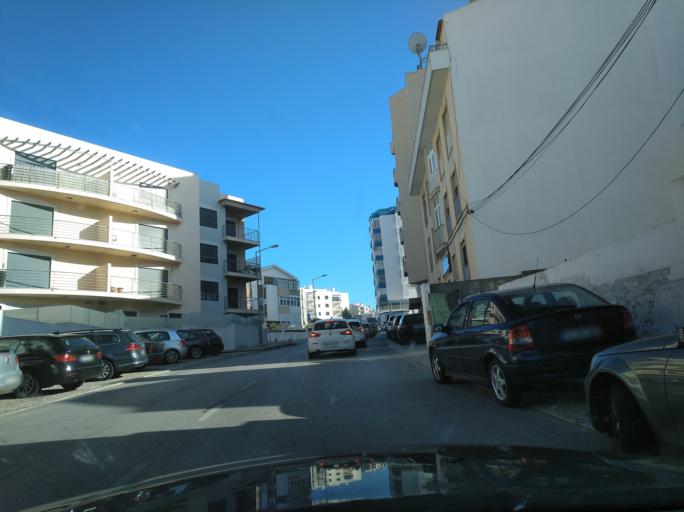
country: PT
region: Lisbon
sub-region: Mafra
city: Ericeira
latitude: 38.9614
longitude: -9.4152
